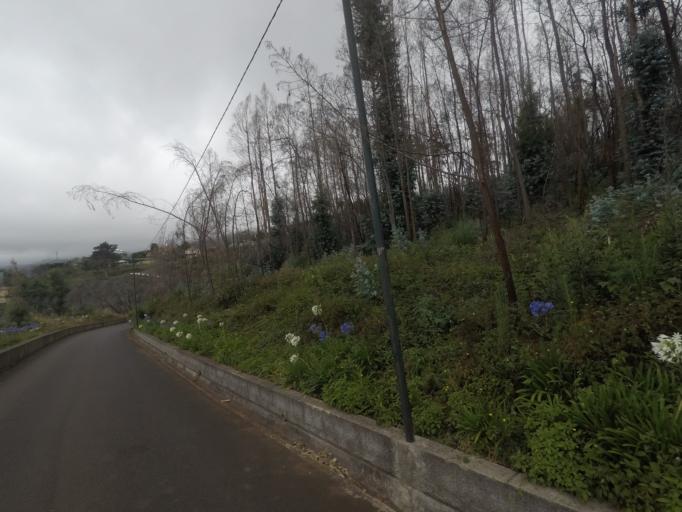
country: PT
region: Madeira
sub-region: Funchal
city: Nossa Senhora do Monte
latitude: 32.6664
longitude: -16.8871
